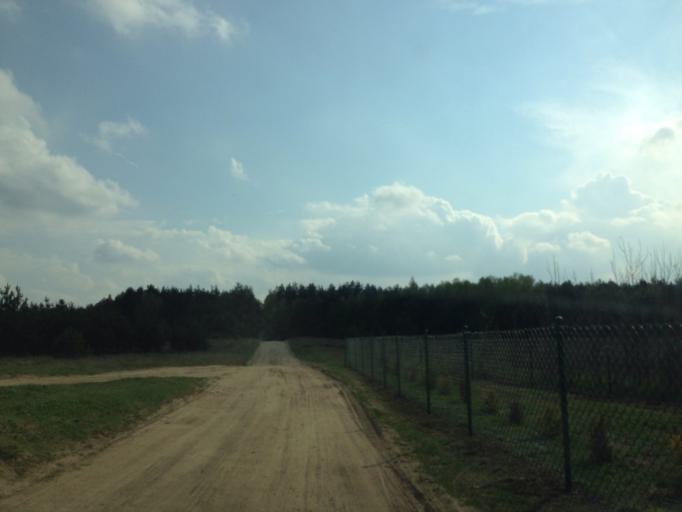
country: PL
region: Kujawsko-Pomorskie
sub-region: Powiat brodnicki
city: Gorzno
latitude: 53.1539
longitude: 19.6516
